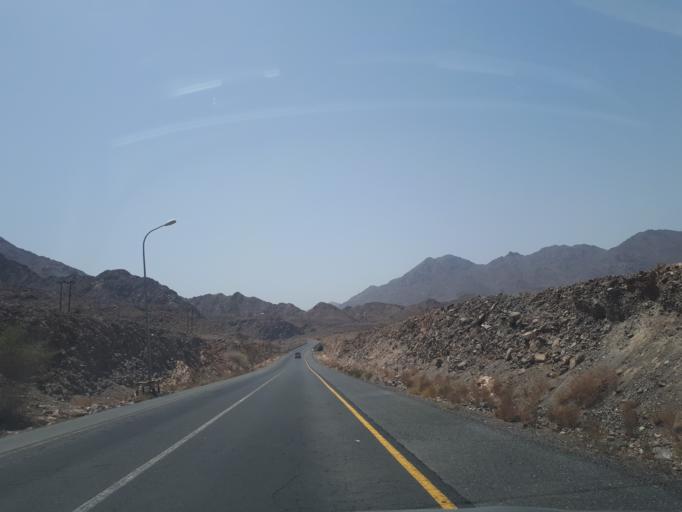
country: OM
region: Muhafazat ad Dakhiliyah
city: Sufalat Sama'il
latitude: 23.1852
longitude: 58.0963
